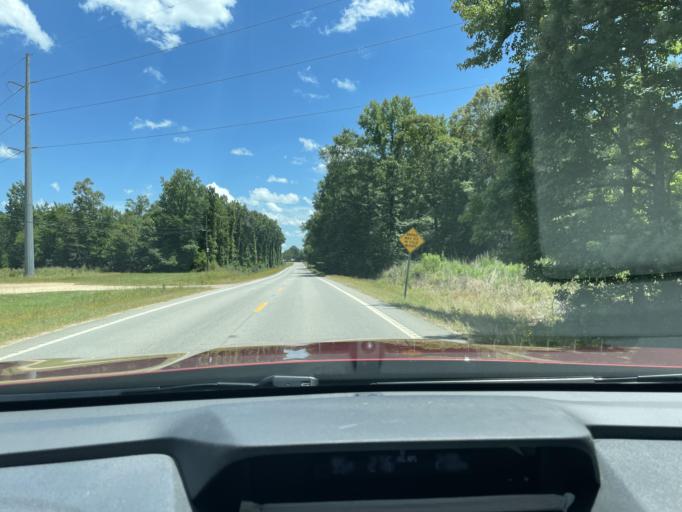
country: US
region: Arkansas
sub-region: Drew County
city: Monticello
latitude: 33.6097
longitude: -91.7387
